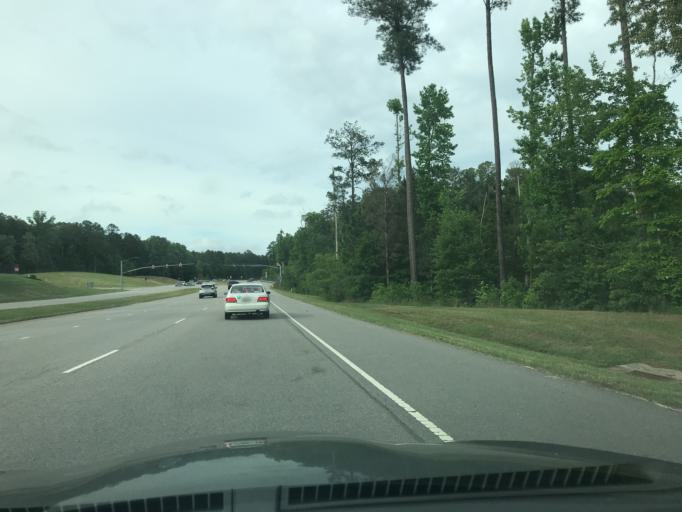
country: US
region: North Carolina
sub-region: Wake County
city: Morrisville
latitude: 35.8646
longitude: -78.8718
